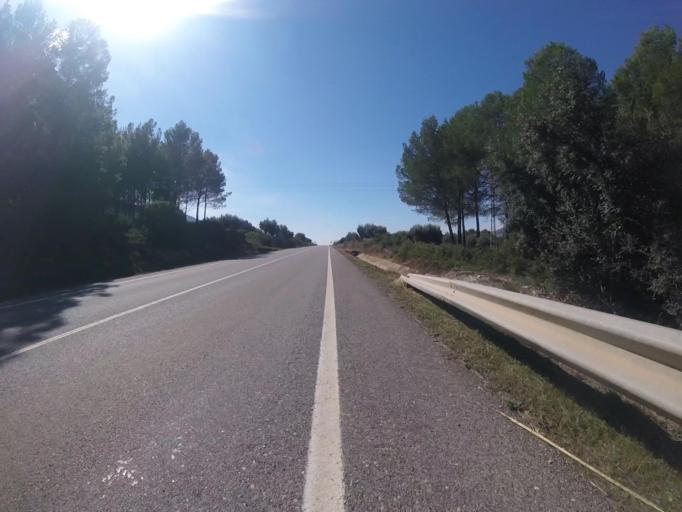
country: ES
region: Valencia
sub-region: Provincia de Castello
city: Sierra-Engarceran
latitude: 40.3190
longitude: -0.0282
